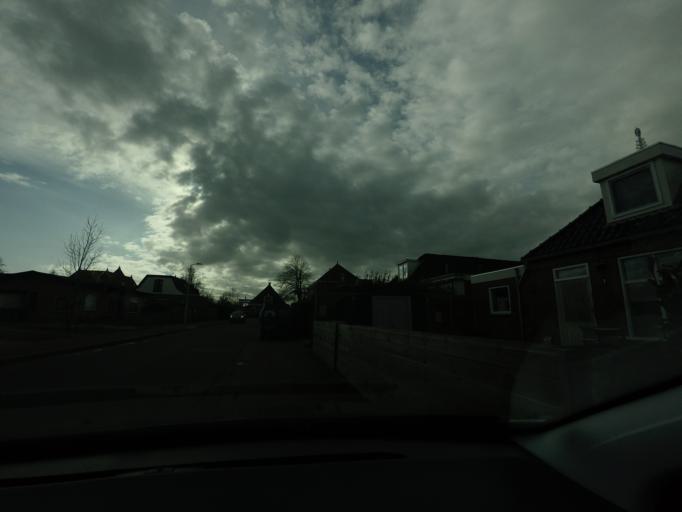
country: NL
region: Friesland
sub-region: Gemeente Boarnsterhim
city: Jirnsum
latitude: 53.0832
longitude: 5.7949
